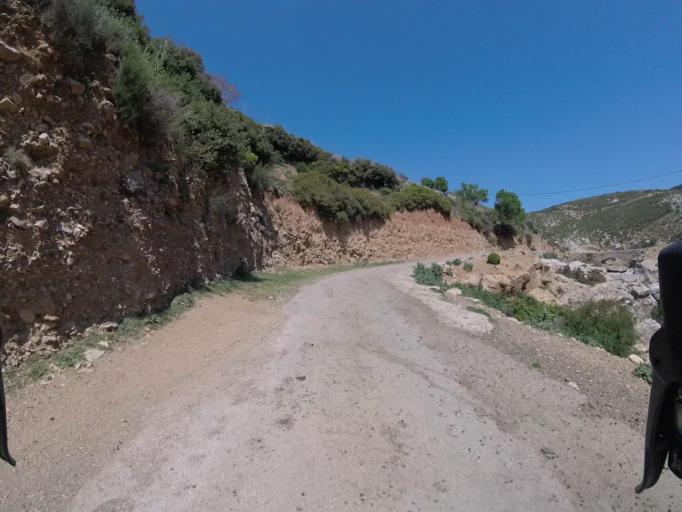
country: ES
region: Valencia
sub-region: Provincia de Castello
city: Sierra-Engarceran
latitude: 40.2618
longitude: -0.0239
